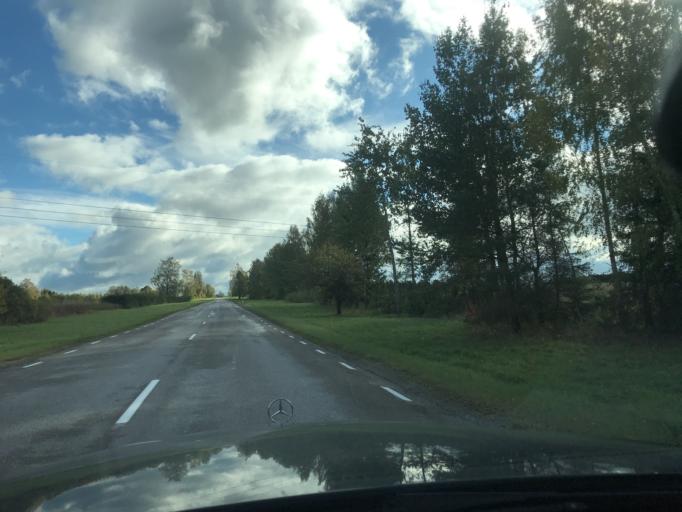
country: EE
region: Valgamaa
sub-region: Torva linn
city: Torva
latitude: 58.0122
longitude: 26.1759
